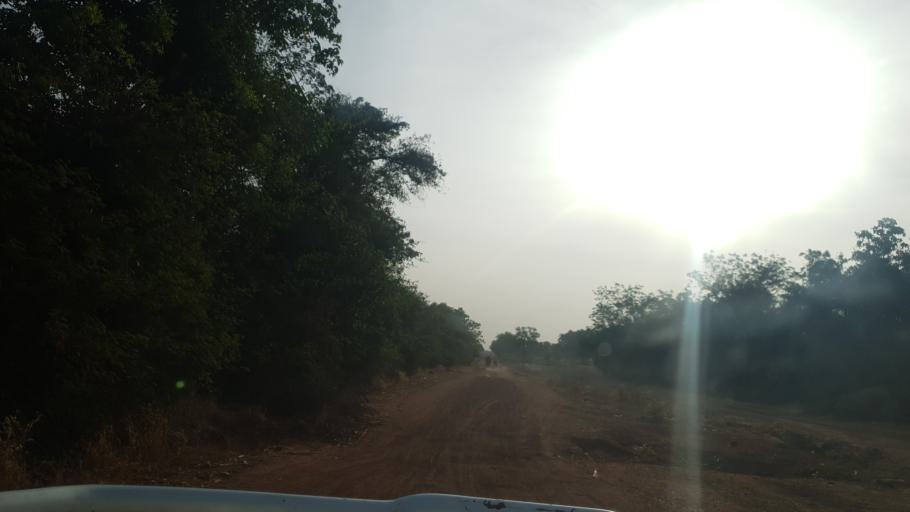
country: ML
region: Koulikoro
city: Dioila
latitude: 12.7709
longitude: -6.9336
